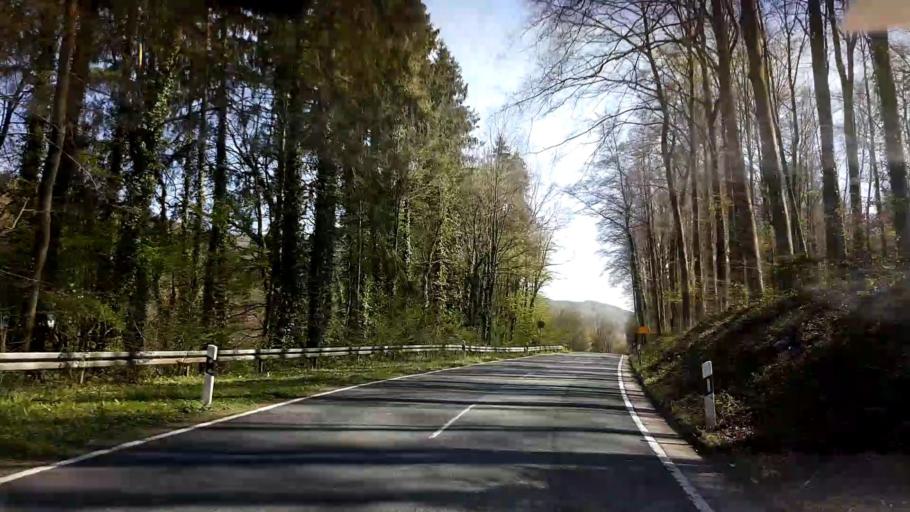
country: DE
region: Bavaria
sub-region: Upper Franconia
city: Unterleinleiter
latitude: 49.8277
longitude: 11.1882
